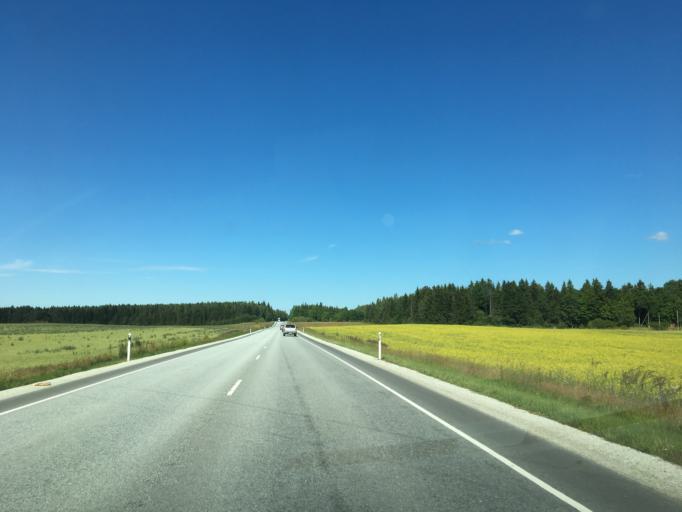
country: EE
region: Harju
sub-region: Keila linn
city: Keila
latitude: 59.2129
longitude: 24.4319
